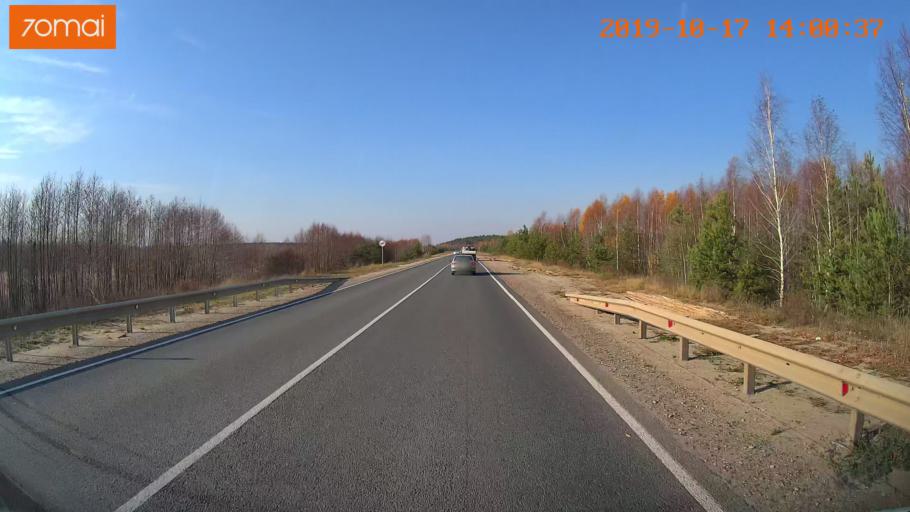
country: RU
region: Rjazan
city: Spas-Klepiki
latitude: 55.1470
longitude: 40.1772
